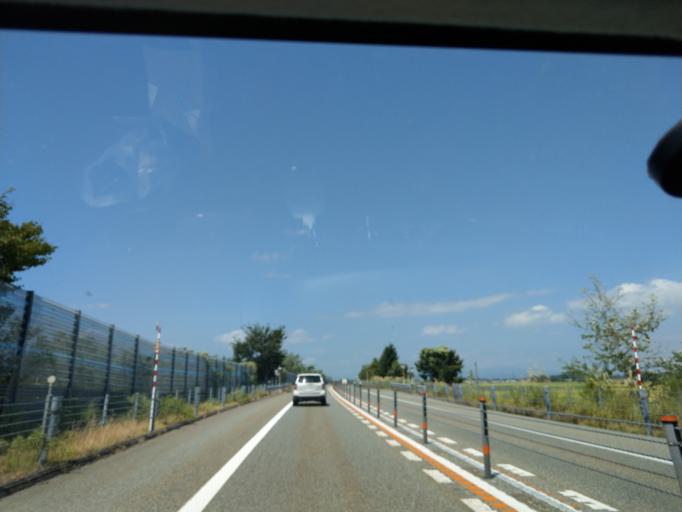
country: JP
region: Akita
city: Omagari
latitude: 39.3807
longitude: 140.4802
